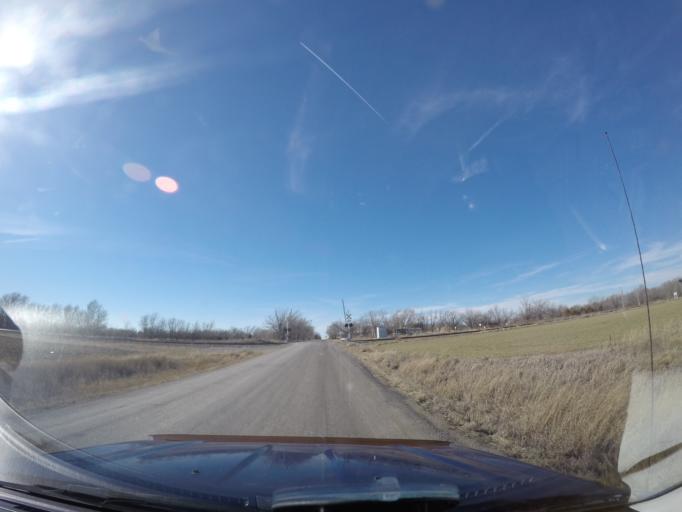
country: US
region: Kansas
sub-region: Dickinson County
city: Herington
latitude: 38.5660
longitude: -96.9618
